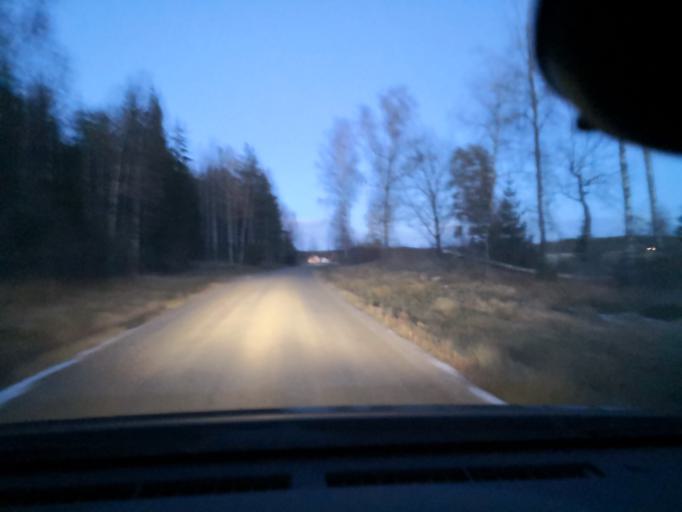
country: SE
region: Vaestmanland
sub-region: Sala Kommun
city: Sala
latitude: 59.8712
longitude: 16.6857
